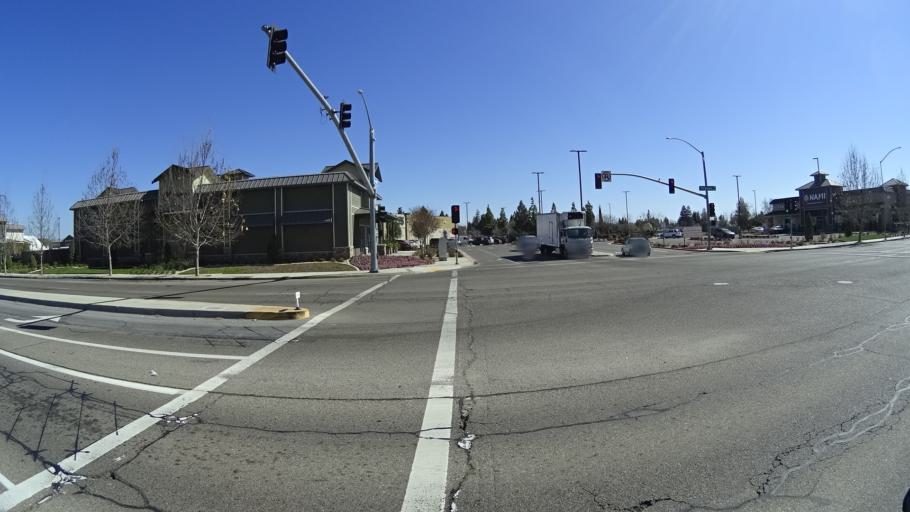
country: US
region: California
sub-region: Fresno County
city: Clovis
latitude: 36.8556
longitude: -119.7844
